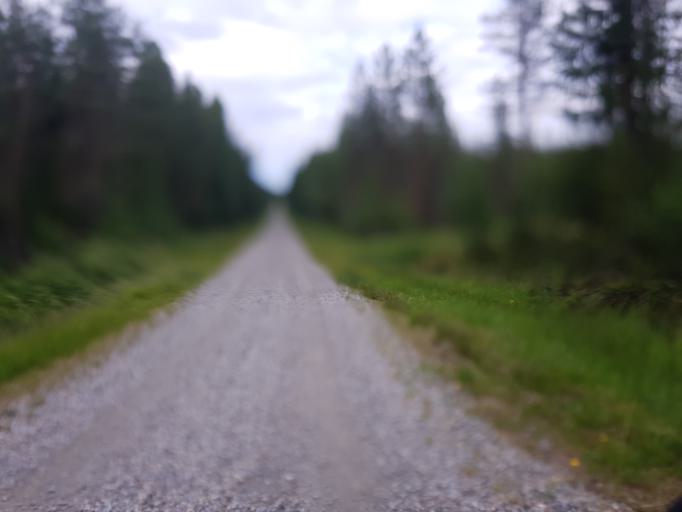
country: FI
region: Kainuu
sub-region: Kehys-Kainuu
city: Kuhmo
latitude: 64.4499
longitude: 29.6921
